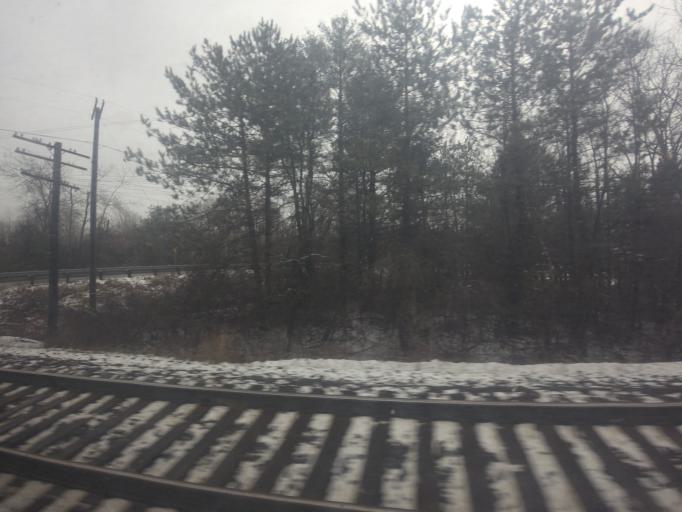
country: CA
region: Ontario
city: Quinte West
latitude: 44.1046
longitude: -77.6083
